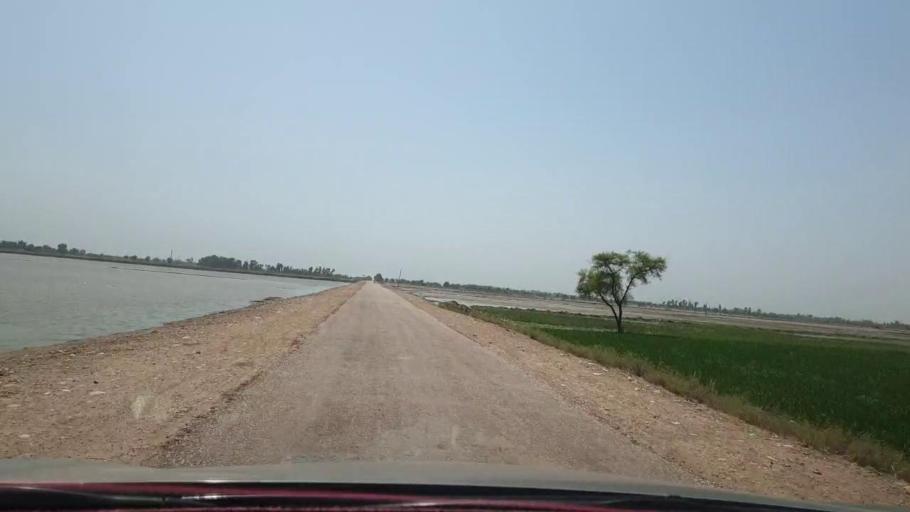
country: PK
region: Sindh
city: Warah
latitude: 27.5486
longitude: 67.7948
